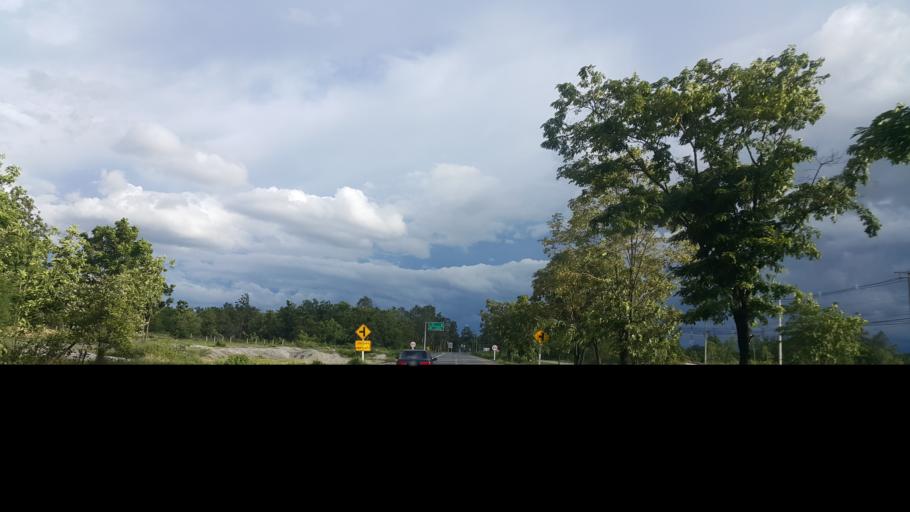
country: TH
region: Tak
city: Ban Tak
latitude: 16.9655
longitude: 99.1314
